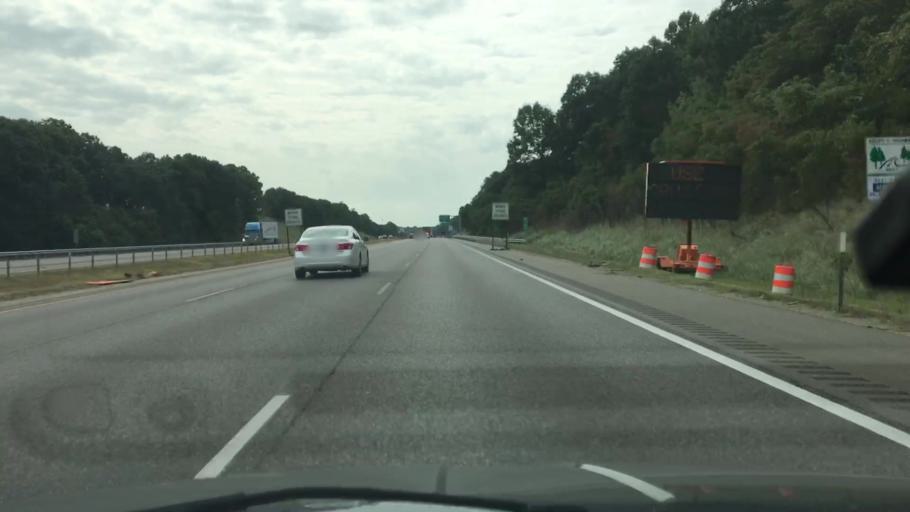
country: US
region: Michigan
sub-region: Berrien County
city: Bridgman
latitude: 41.9505
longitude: -86.5625
